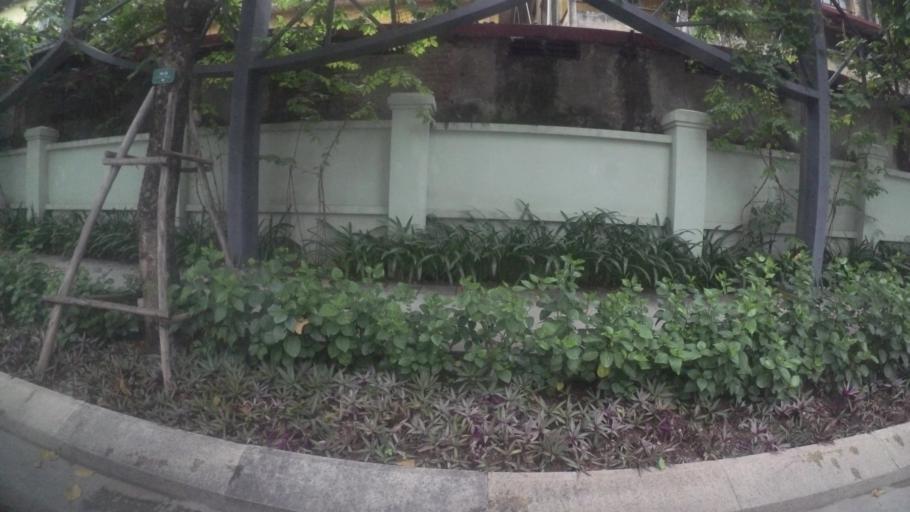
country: VN
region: Ha Noi
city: Cau Dien
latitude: 21.0386
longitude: 105.7613
